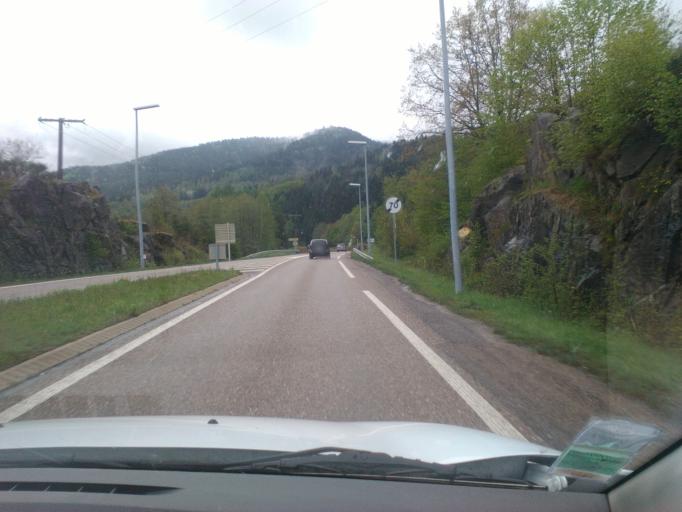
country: FR
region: Lorraine
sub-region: Departement des Vosges
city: Saulxures-sur-Moselotte
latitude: 47.9551
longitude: 6.7447
